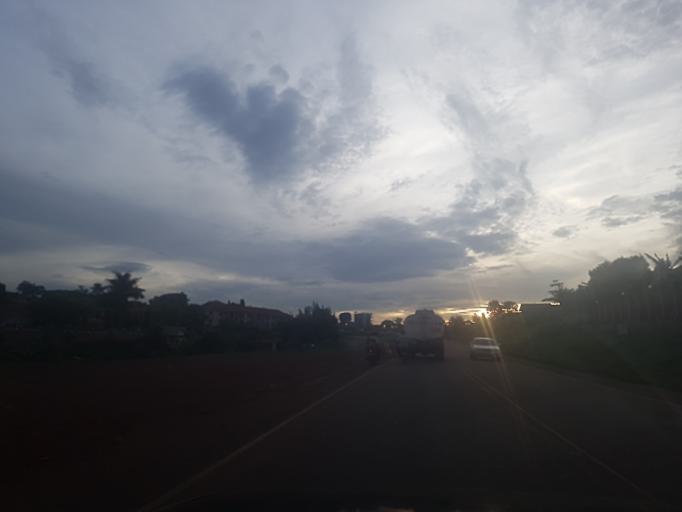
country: UG
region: Central Region
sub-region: Wakiso District
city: Kireka
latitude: 0.3656
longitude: 32.6092
